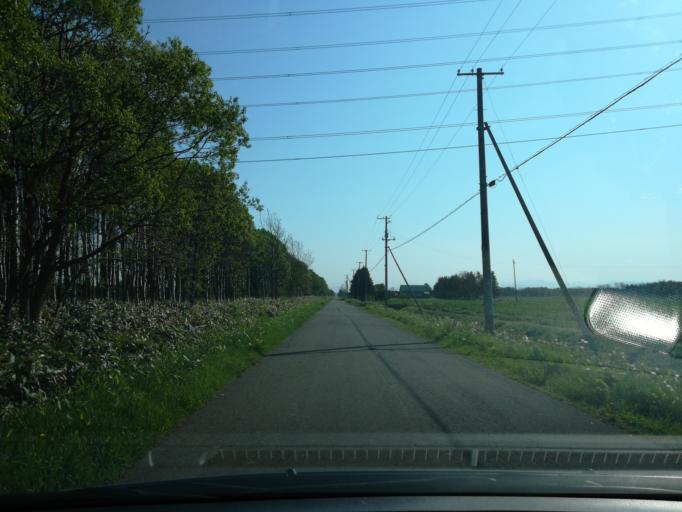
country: JP
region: Hokkaido
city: Ebetsu
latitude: 43.1111
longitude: 141.6373
